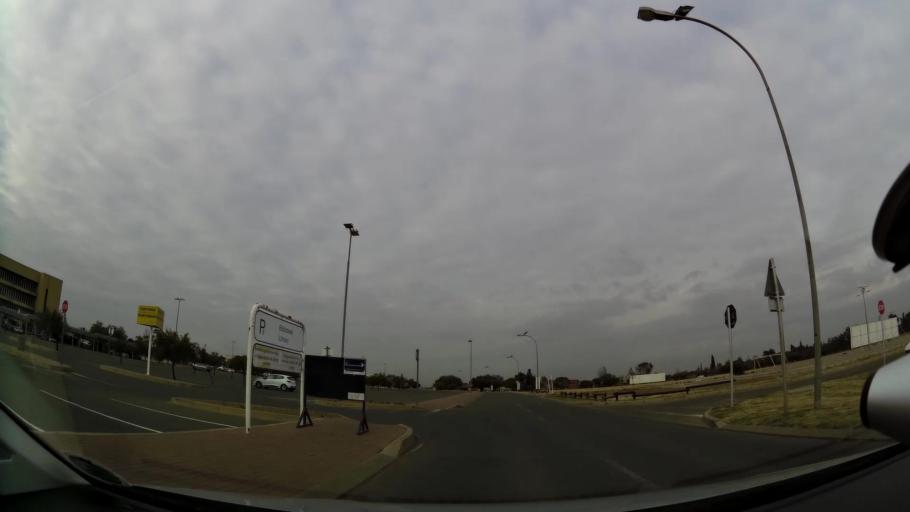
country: ZA
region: Orange Free State
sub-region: Mangaung Metropolitan Municipality
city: Bloemfontein
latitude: -29.1090
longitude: 26.1814
